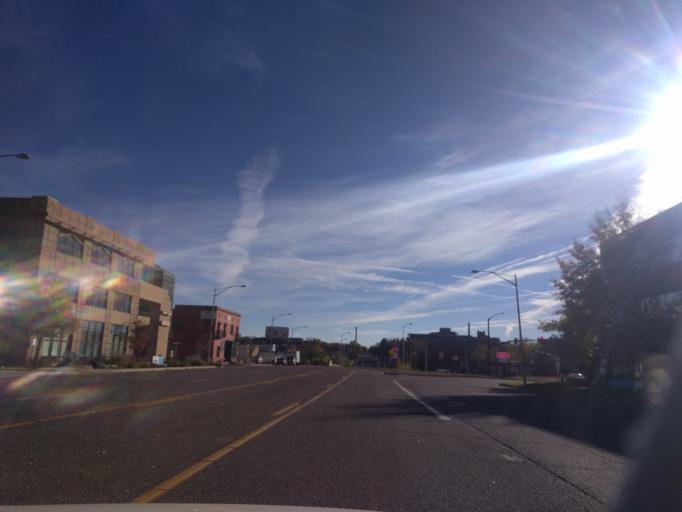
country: US
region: Colorado
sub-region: El Paso County
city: Colorado Springs
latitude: 38.8337
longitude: -104.8165
